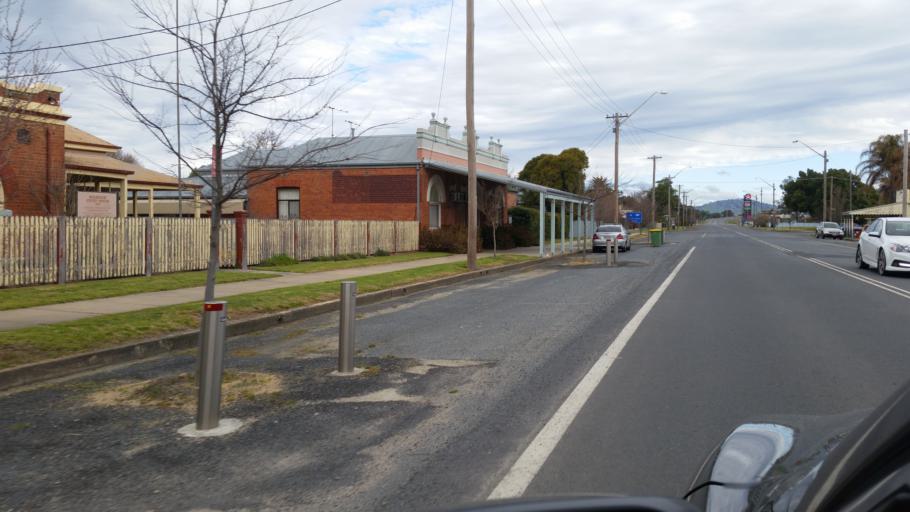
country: AU
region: New South Wales
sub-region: Greater Hume Shire
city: Holbrook
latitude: -35.7269
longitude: 147.3117
